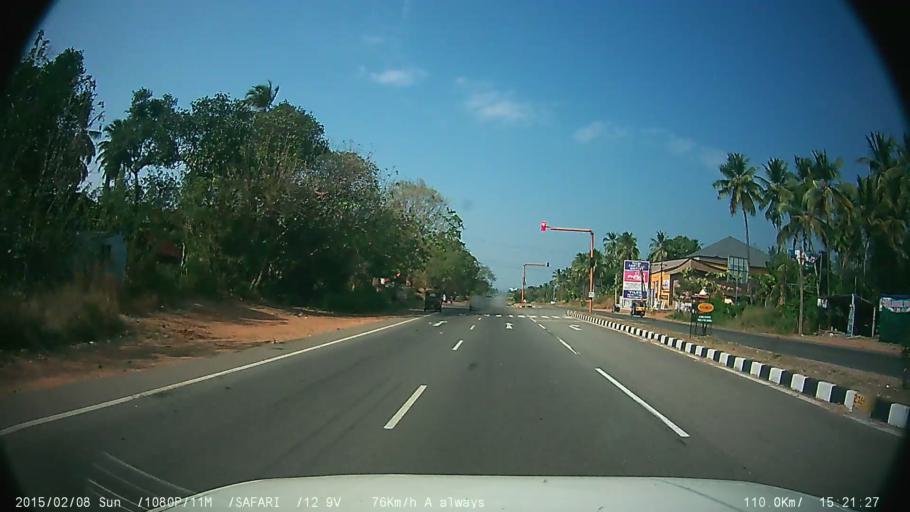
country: IN
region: Kerala
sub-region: Thrissur District
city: Trichur
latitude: 10.4768
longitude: 76.2577
